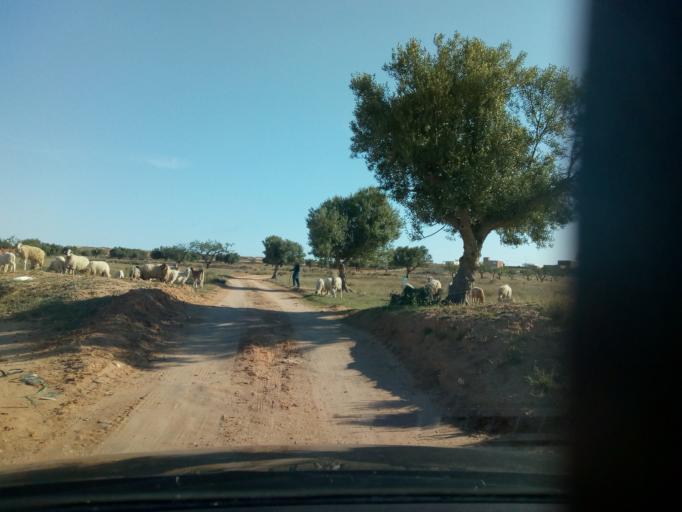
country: TN
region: Safaqis
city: Sfax
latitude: 34.7253
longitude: 10.6127
